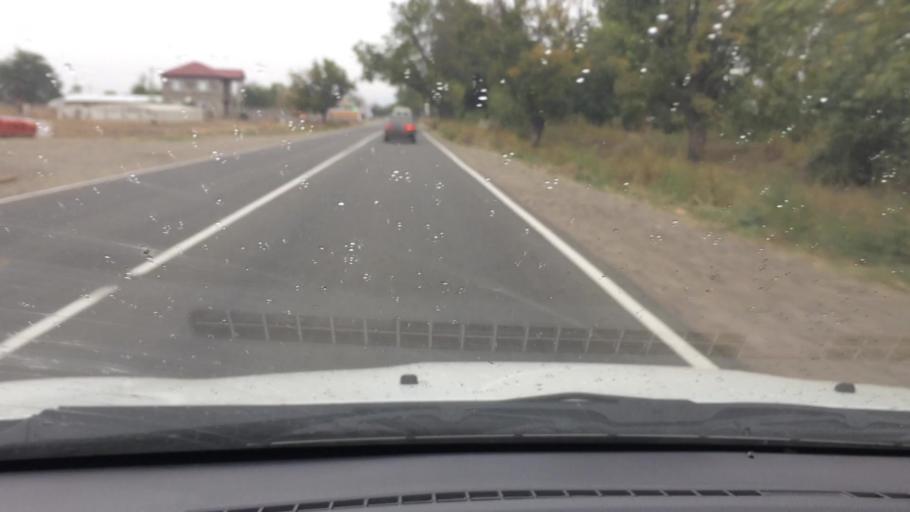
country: GE
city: Naghvarevi
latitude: 41.3964
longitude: 44.8264
